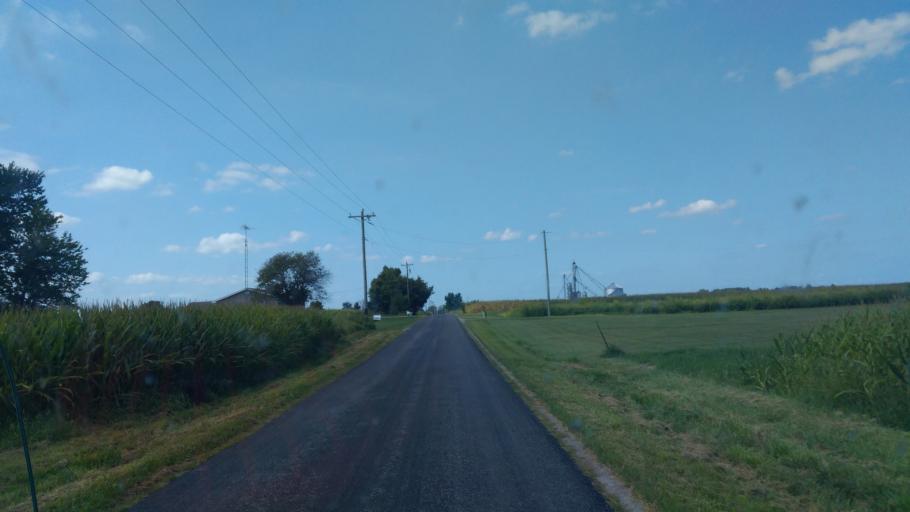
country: US
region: Ohio
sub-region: Union County
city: Richwood
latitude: 40.4549
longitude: -83.3939
